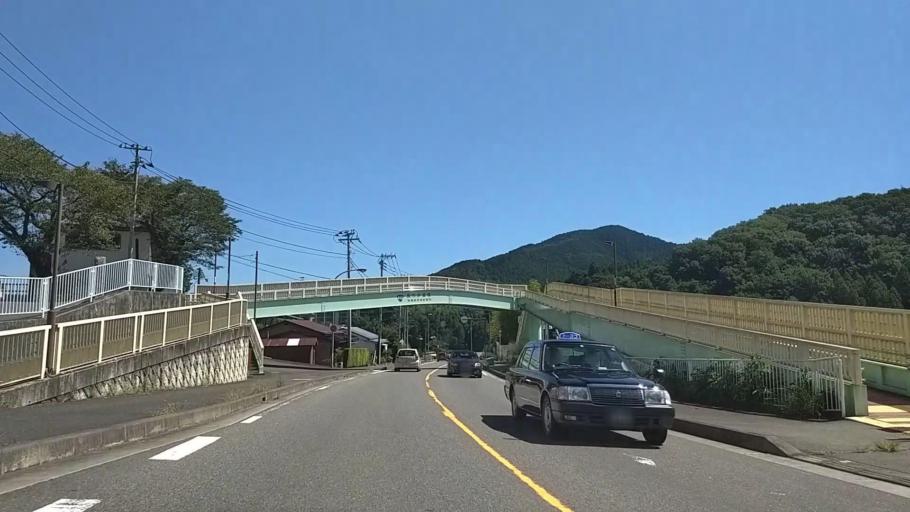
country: JP
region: Tokyo
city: Hachioji
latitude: 35.5658
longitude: 139.2581
